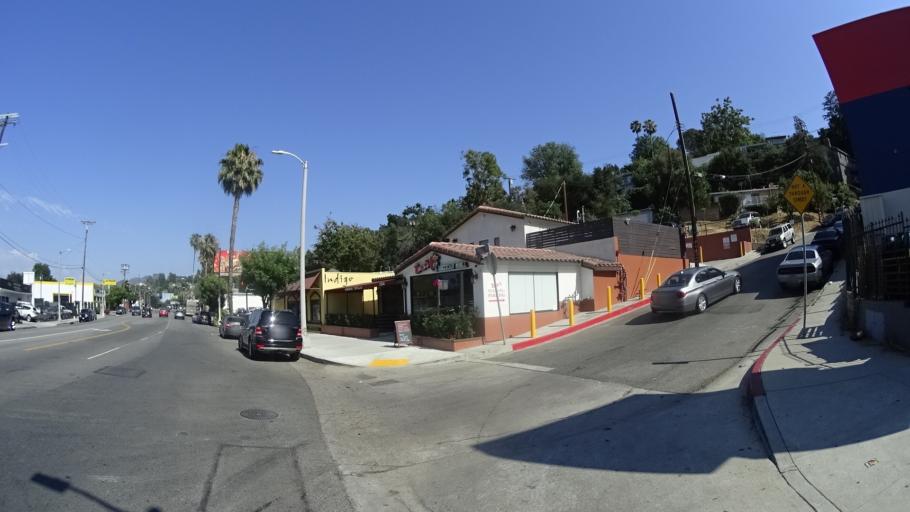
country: US
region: California
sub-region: Los Angeles County
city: Universal City
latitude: 34.1398
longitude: -118.3837
